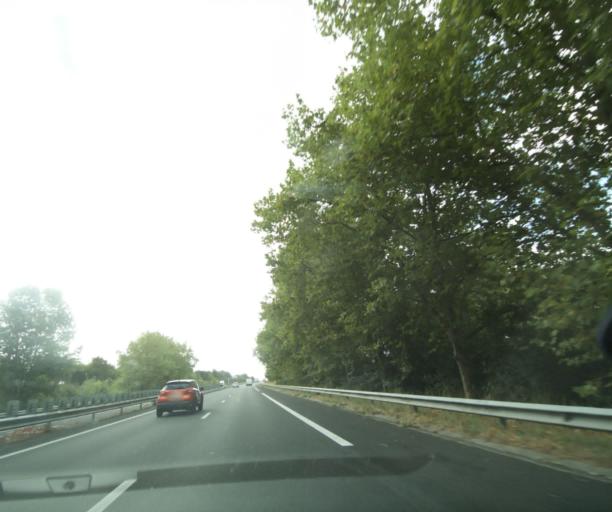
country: FR
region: Poitou-Charentes
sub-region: Departement de la Charente-Maritime
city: Chermignac
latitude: 45.7043
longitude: -0.6519
